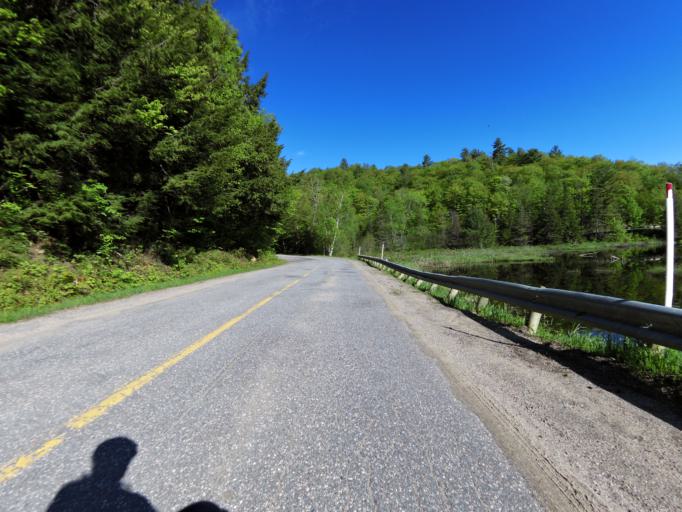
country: CA
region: Quebec
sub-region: Outaouais
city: Wakefield
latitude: 45.6018
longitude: -75.8621
